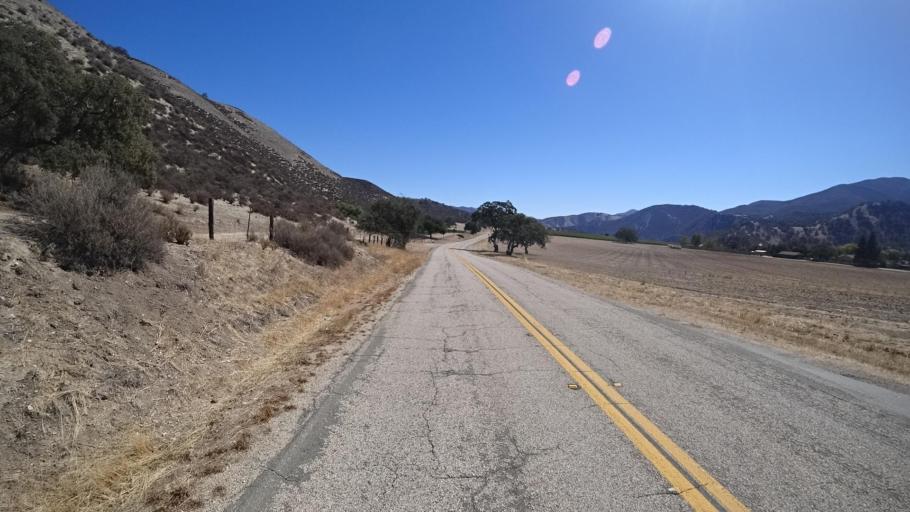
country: US
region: California
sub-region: Monterey County
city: Greenfield
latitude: 36.2705
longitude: -121.3917
